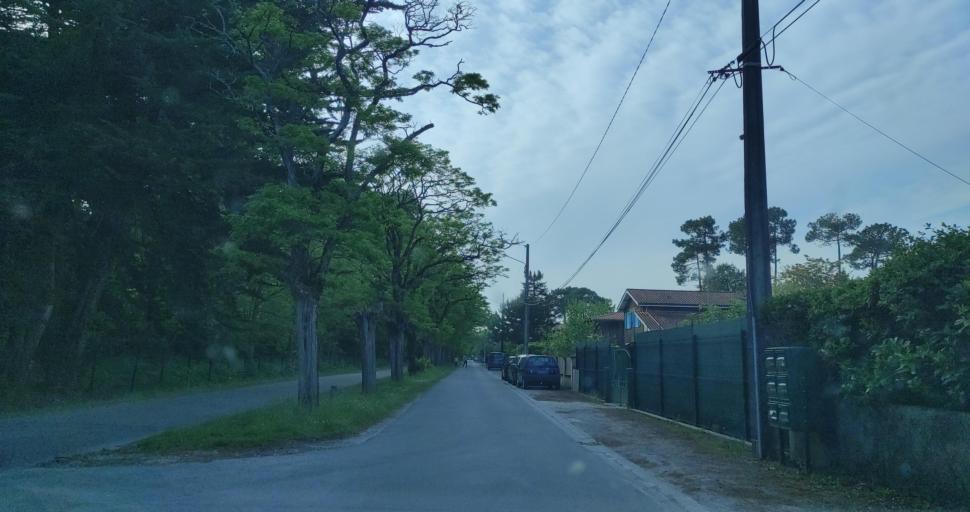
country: FR
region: Aquitaine
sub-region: Departement de la Gironde
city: Ares
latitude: 44.7549
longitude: -1.1299
